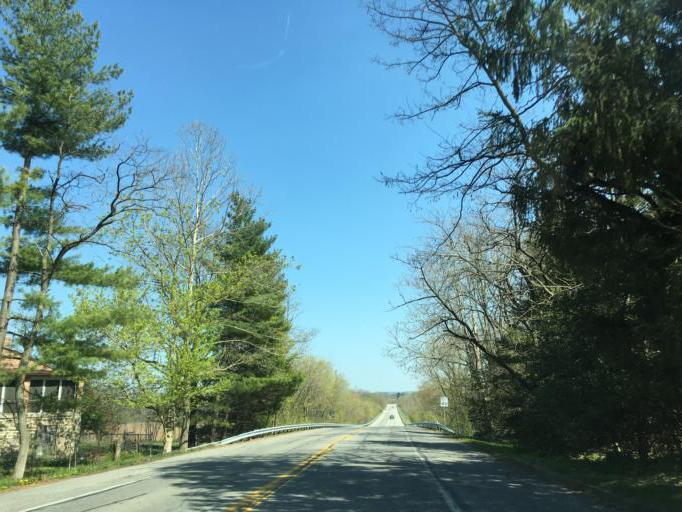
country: US
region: Maryland
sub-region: Frederick County
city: Walkersville
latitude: 39.5091
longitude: -77.3873
